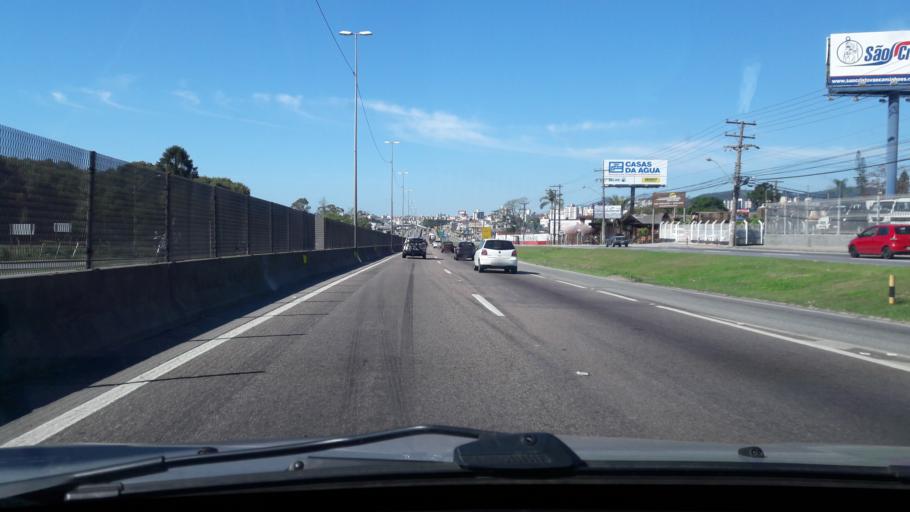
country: BR
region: Santa Catarina
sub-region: Sao Jose
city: Campinas
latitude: -27.5467
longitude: -48.6198
